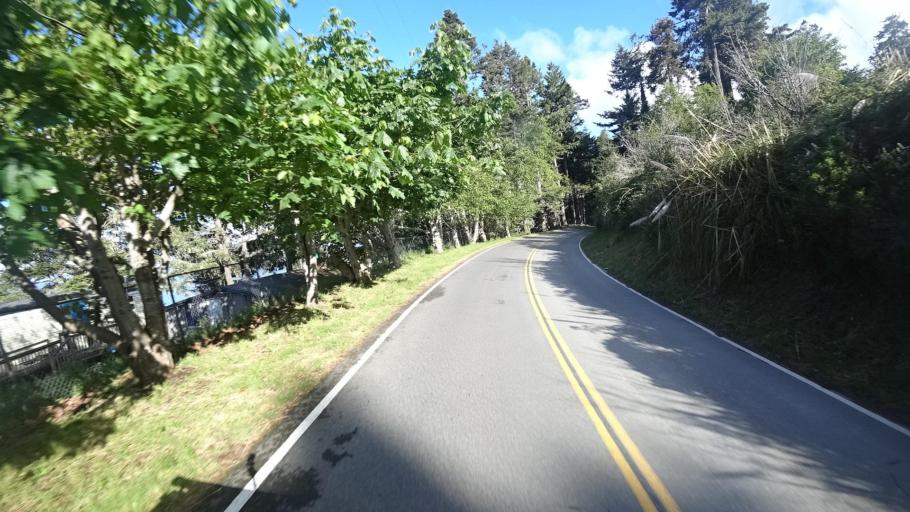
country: US
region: California
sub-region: Humboldt County
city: Westhaven-Moonstone
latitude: 41.0525
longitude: -124.1297
